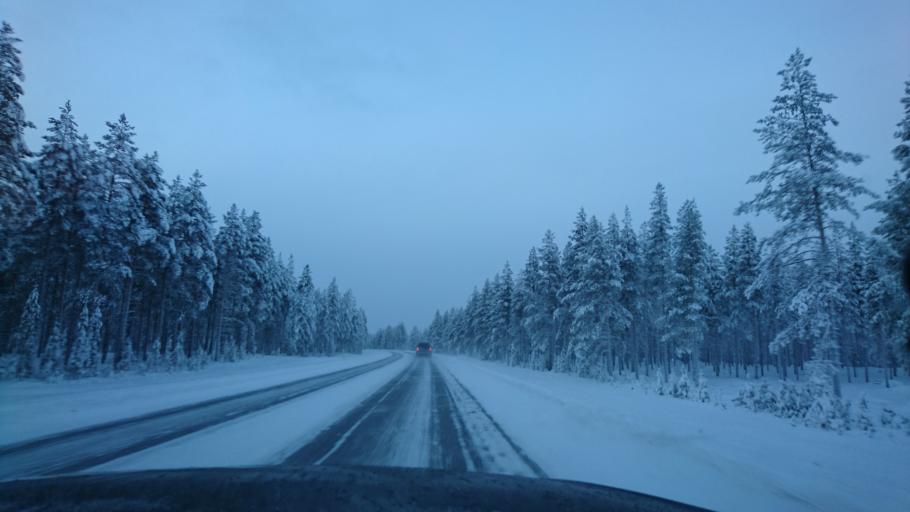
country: FI
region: Kainuu
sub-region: Kehys-Kainuu
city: Puolanka
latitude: 65.4291
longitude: 27.5194
